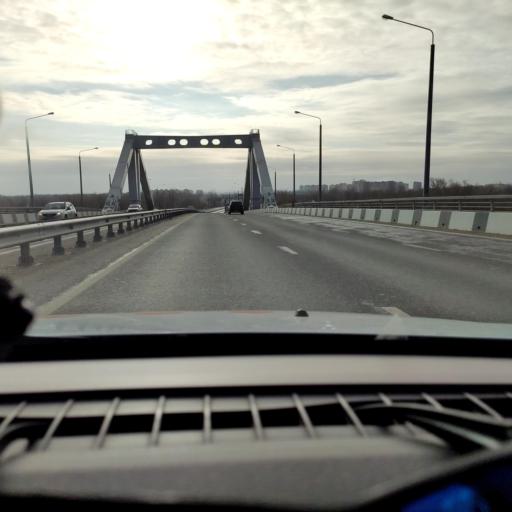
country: RU
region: Samara
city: Rozhdestveno
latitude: 53.1747
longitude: 50.0857
